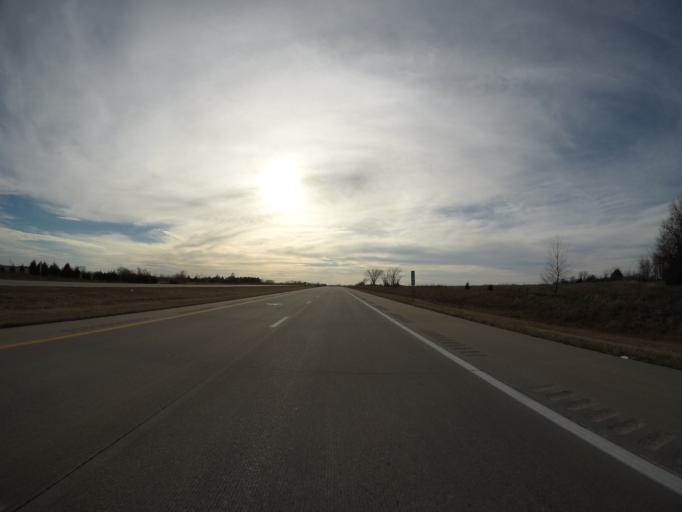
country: US
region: Kansas
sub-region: Franklin County
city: Wellsville
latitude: 38.6844
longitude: -95.1224
